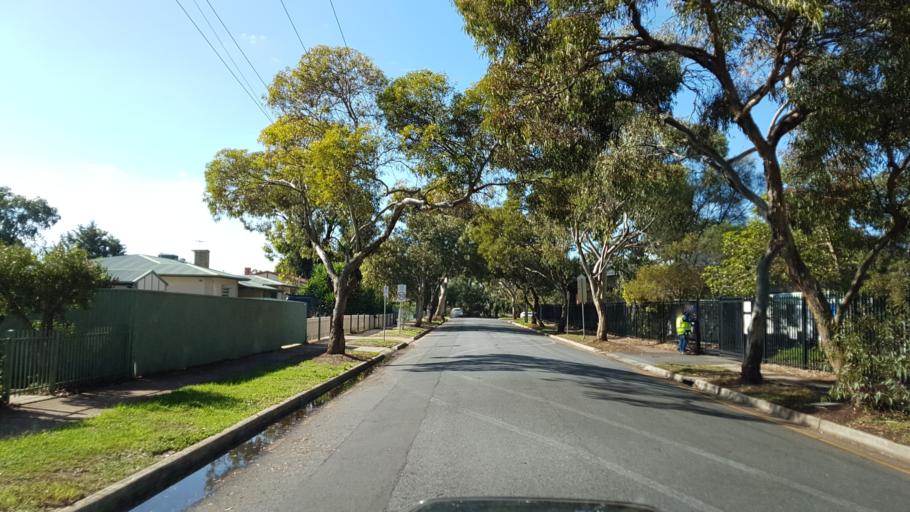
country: AU
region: South Australia
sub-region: Salisbury
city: Salisbury
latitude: -34.7546
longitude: 138.6404
